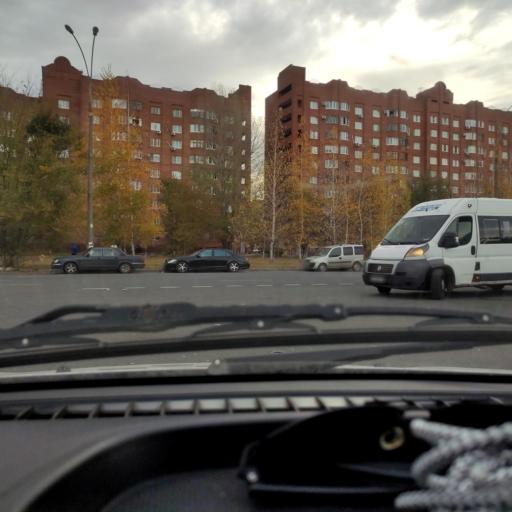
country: RU
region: Samara
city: Tol'yatti
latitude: 53.5042
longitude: 49.2755
